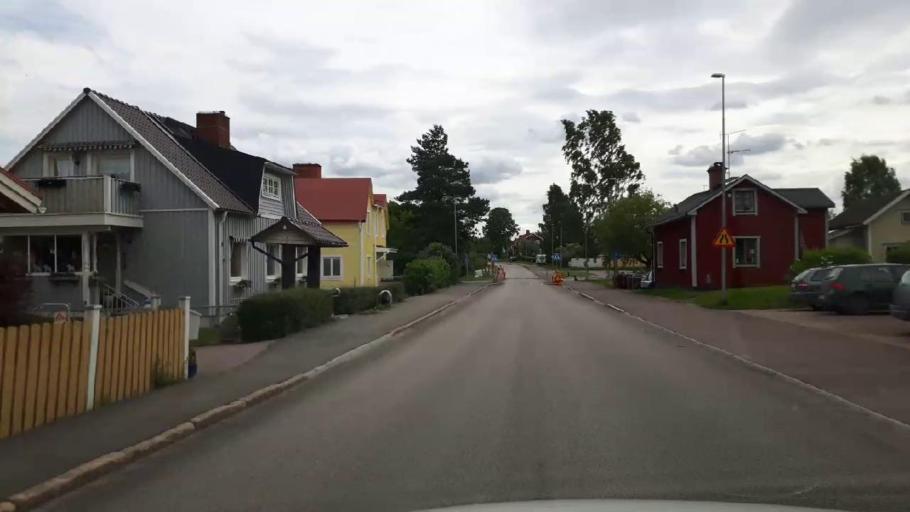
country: SE
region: Dalarna
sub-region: Hedemora Kommun
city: Hedemora
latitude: 60.2725
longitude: 15.9910
